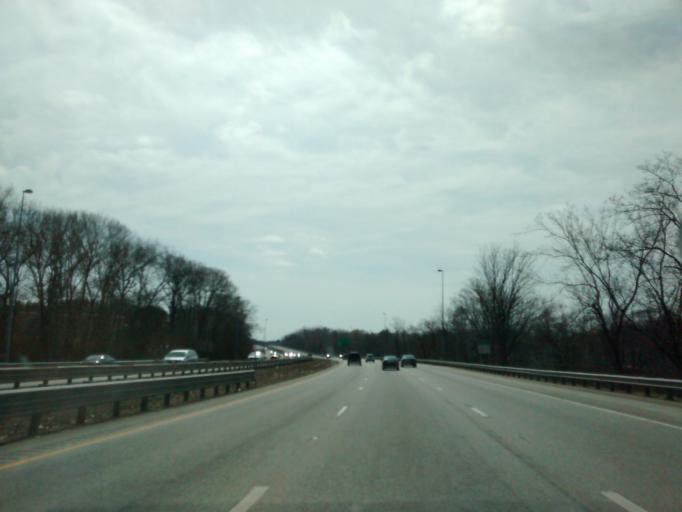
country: US
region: Massachusetts
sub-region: Worcester County
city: Auburn
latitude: 42.2303
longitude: -71.8250
